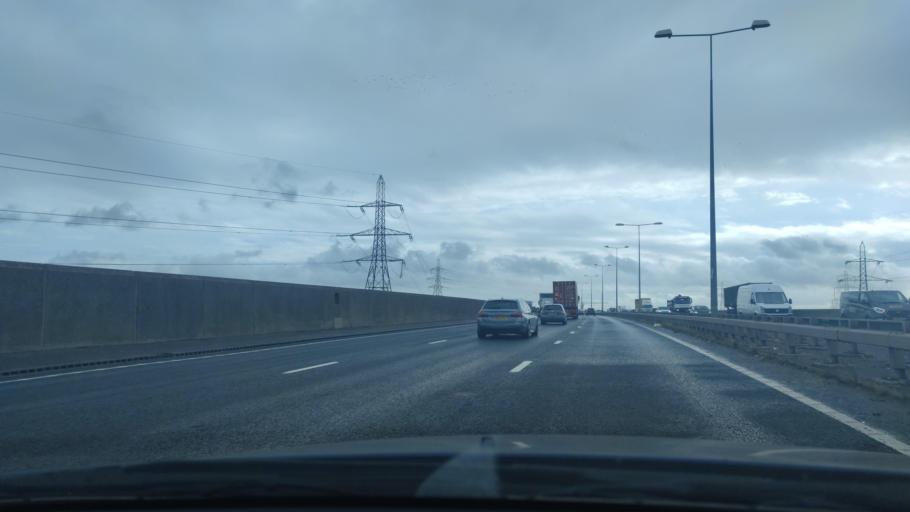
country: GB
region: England
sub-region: Essex
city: Purfleet
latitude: 51.5020
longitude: 0.2146
